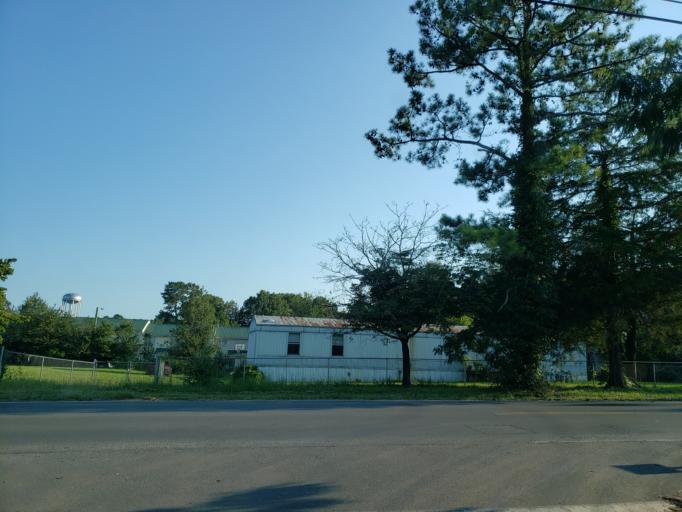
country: US
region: Georgia
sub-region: Murray County
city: Chatsworth
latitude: 34.7538
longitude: -84.8143
